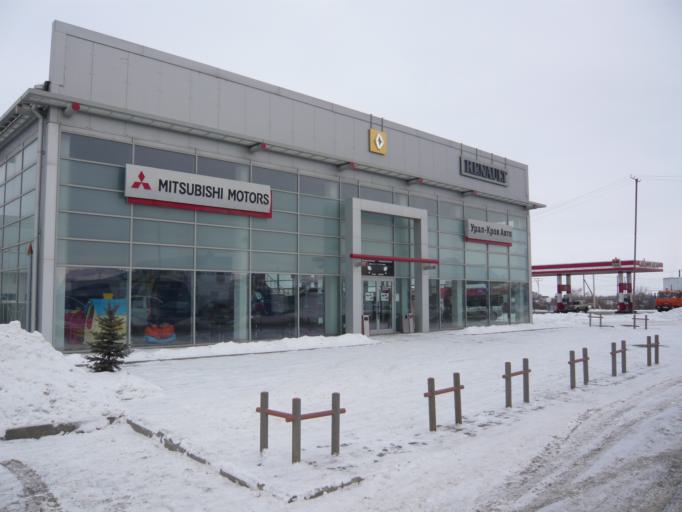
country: KZ
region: Batys Qazaqstan
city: Oral
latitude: 51.2466
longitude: 51.3846
